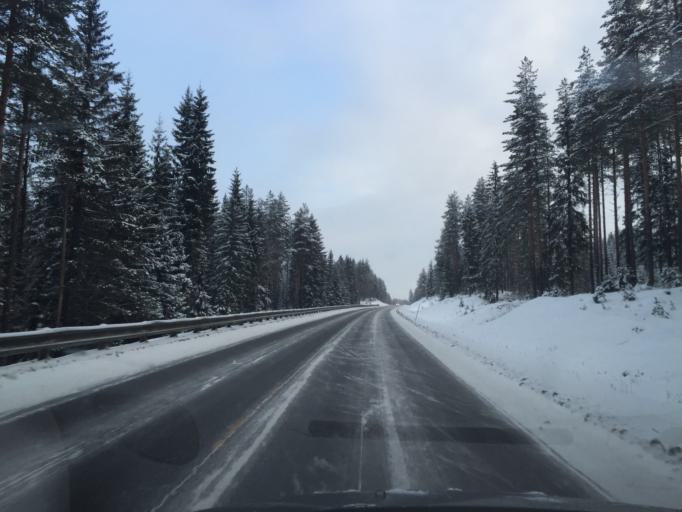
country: NO
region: Hedmark
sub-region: Elverum
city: Elverum
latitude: 60.9570
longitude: 11.7053
